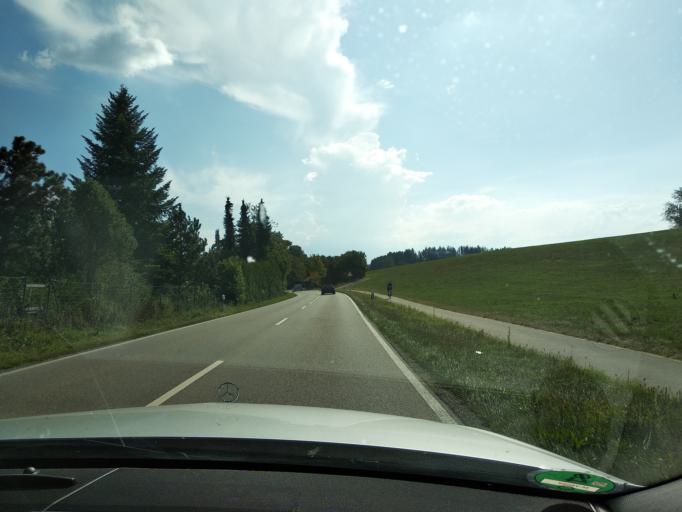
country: DE
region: Baden-Wuerttemberg
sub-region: Tuebingen Region
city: Amtzell
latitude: 47.6832
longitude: 9.7567
